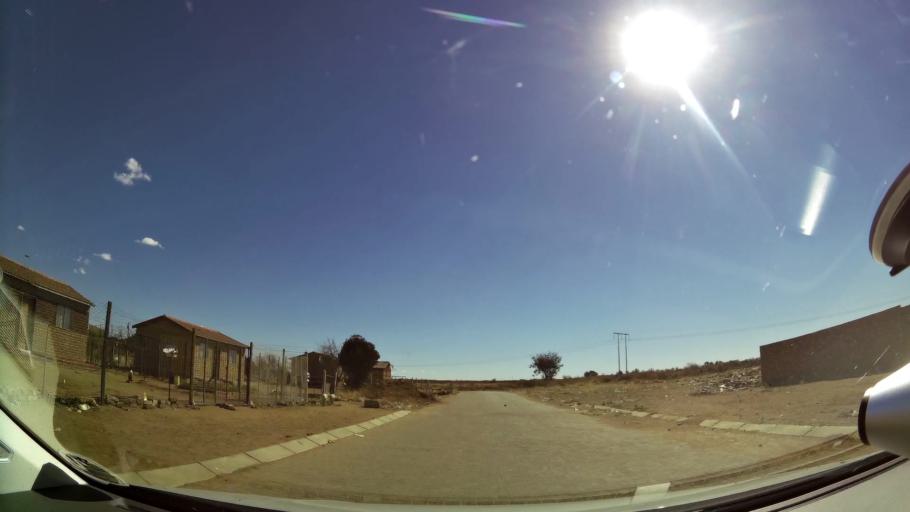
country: ZA
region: North-West
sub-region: Dr Kenneth Kaunda District Municipality
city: Klerksdorp
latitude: -26.8668
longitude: 26.5754
